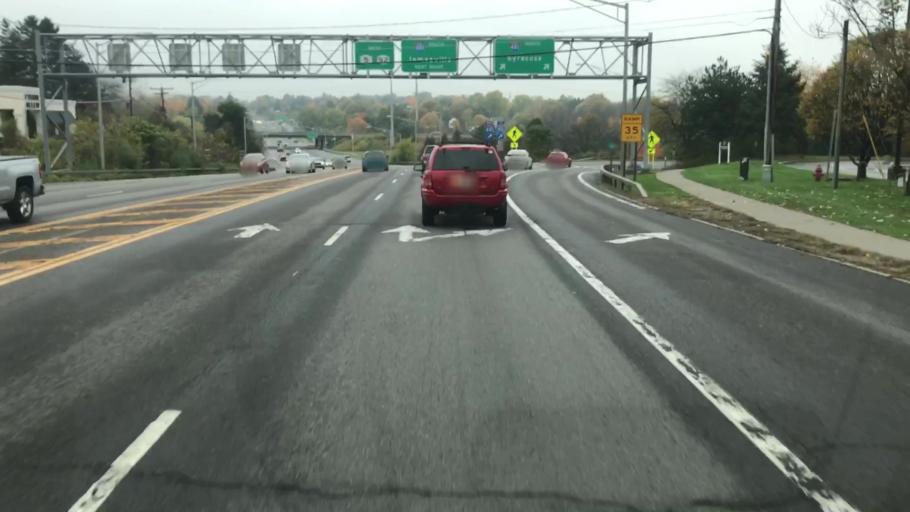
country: US
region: New York
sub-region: Onondaga County
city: East Syracuse
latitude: 43.0321
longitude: -76.0550
